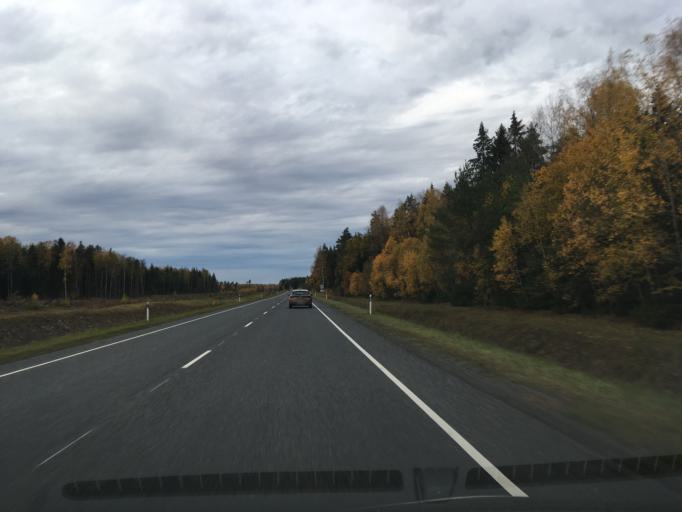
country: EE
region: Harju
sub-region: Nissi vald
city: Turba
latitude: 58.9617
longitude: 24.0729
